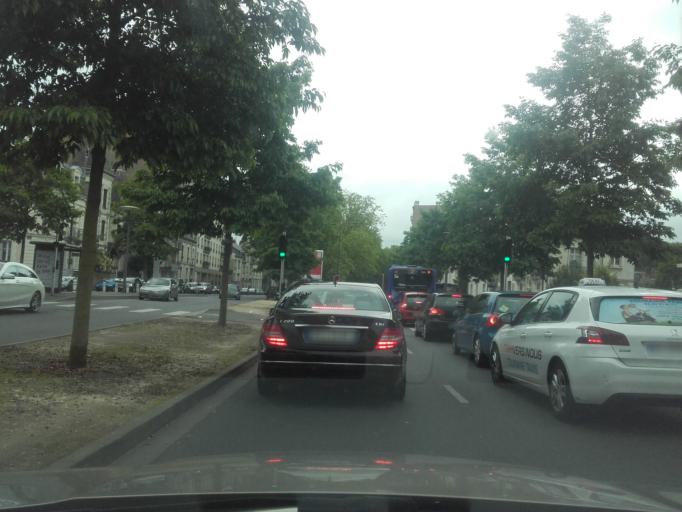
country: FR
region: Centre
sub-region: Departement d'Indre-et-Loire
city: Tours
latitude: 47.3939
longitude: 0.7032
